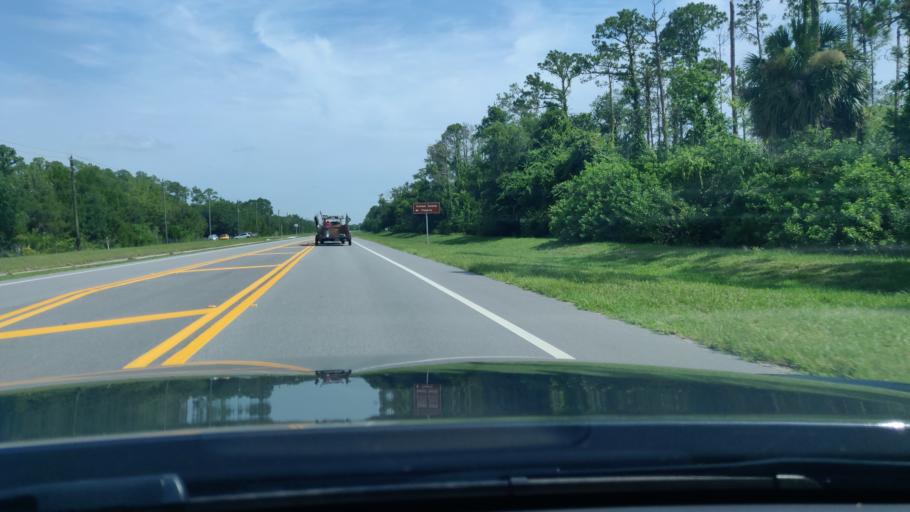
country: US
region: Florida
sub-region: Flagler County
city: Flagler Beach
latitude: 29.5068
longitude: -81.1605
